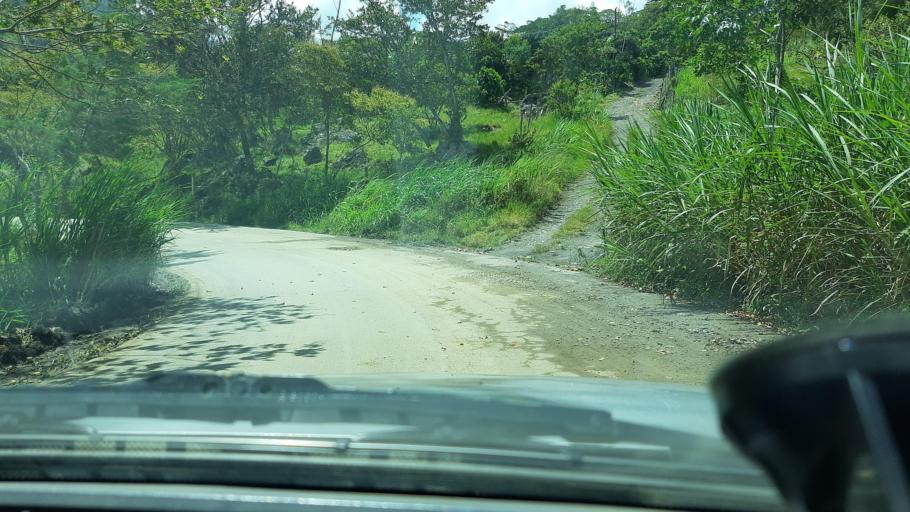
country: CO
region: Boyaca
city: Chinavita
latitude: 5.1775
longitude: -73.3819
